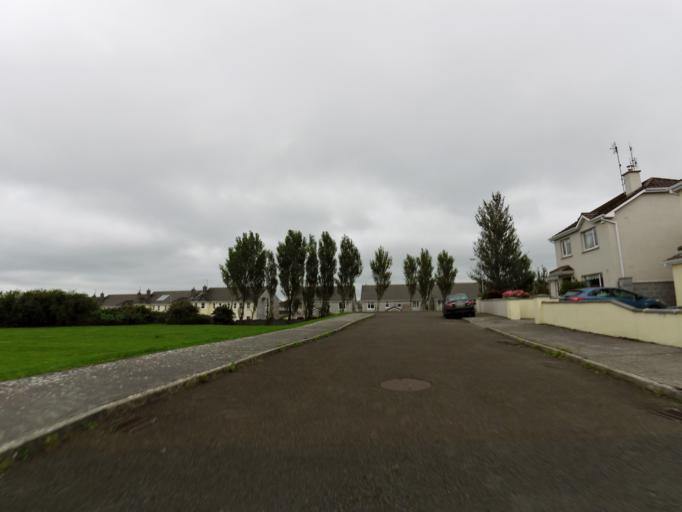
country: IE
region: Connaught
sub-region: County Galway
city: Loughrea
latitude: 53.2026
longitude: -8.5556
